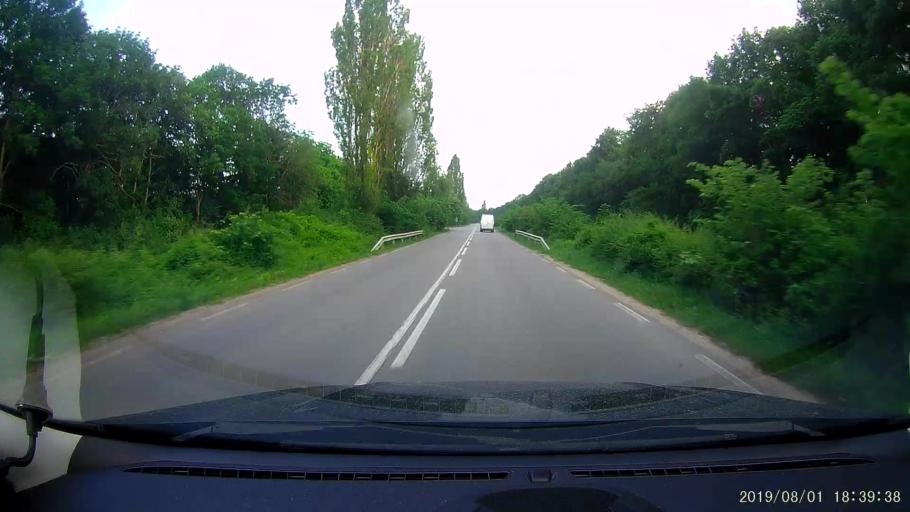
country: BG
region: Shumen
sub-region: Obshtina Khitrino
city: Gara Khitrino
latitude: 43.3817
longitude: 26.9169
